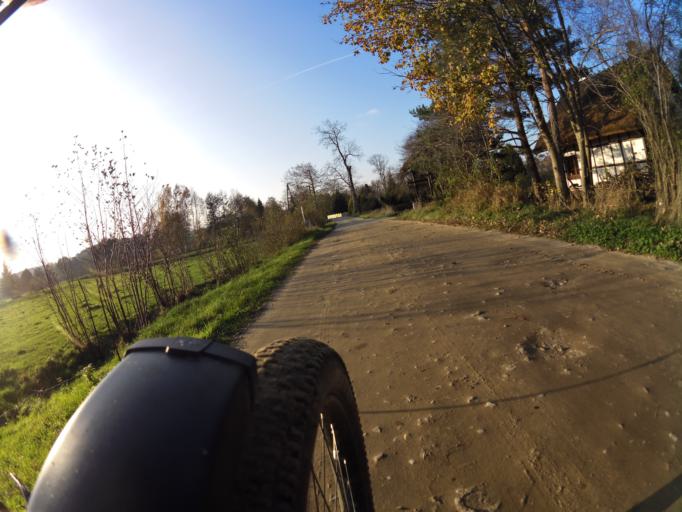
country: PL
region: Pomeranian Voivodeship
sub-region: Powiat pucki
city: Krokowa
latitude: 54.7500
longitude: 18.1940
